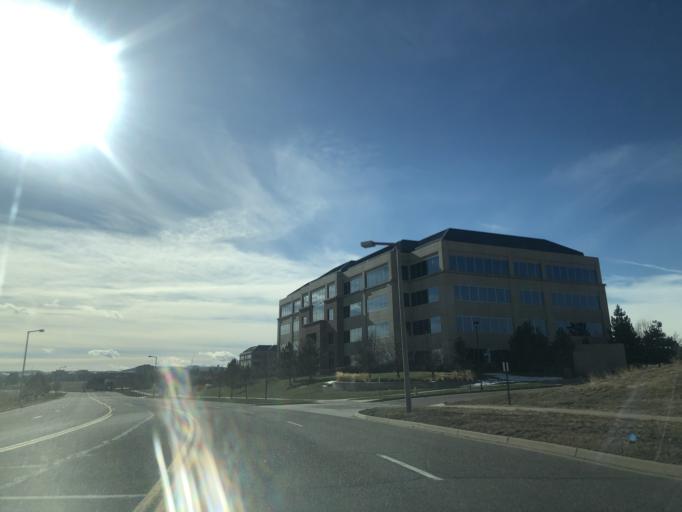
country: US
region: Colorado
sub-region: Douglas County
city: Meridian
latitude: 39.5517
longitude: -104.8658
